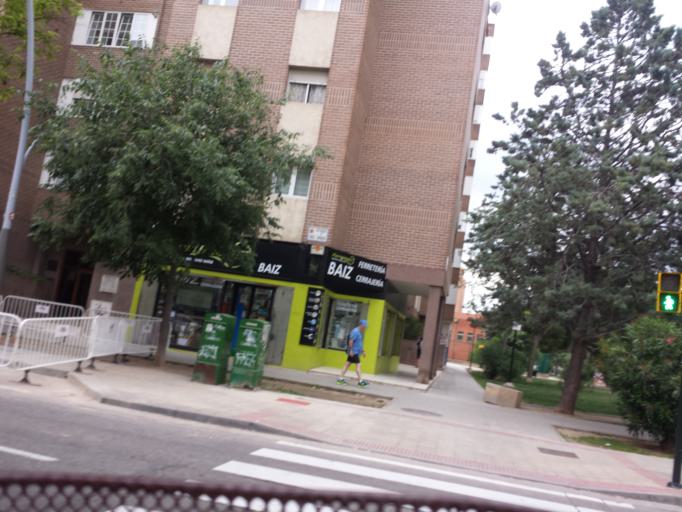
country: ES
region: Aragon
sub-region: Provincia de Zaragoza
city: Almozara
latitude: 41.6619
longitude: -0.9037
